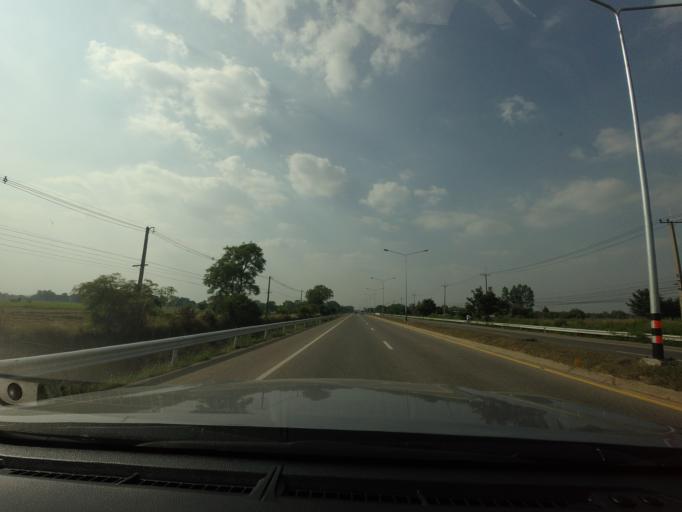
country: TH
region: Sukhothai
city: Sukhothai
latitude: 17.0188
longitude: 99.9035
